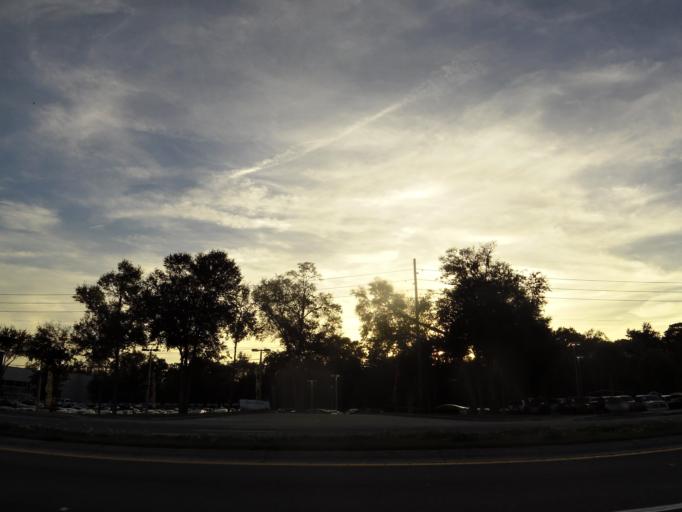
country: US
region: Florida
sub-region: Volusia County
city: De Land Southwest
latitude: 28.9898
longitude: -81.3012
